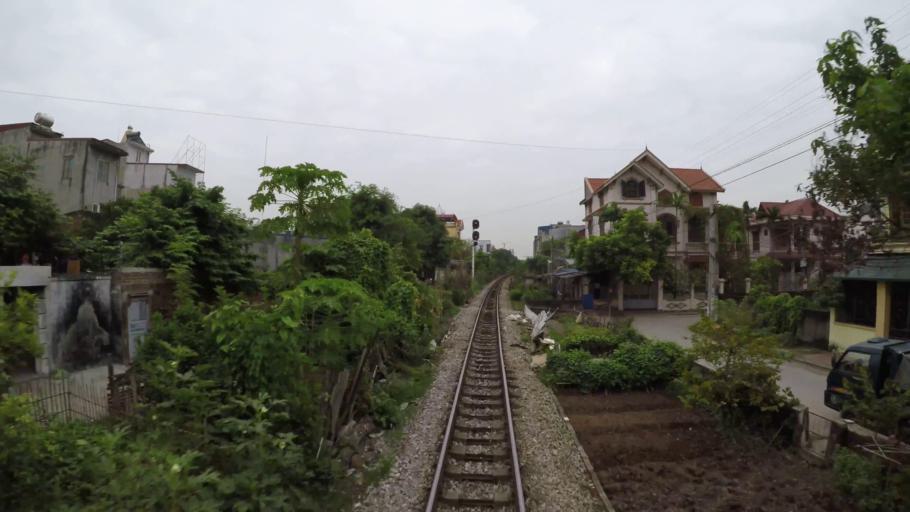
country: VN
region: Hai Phong
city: An Duong
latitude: 20.8858
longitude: 106.6016
